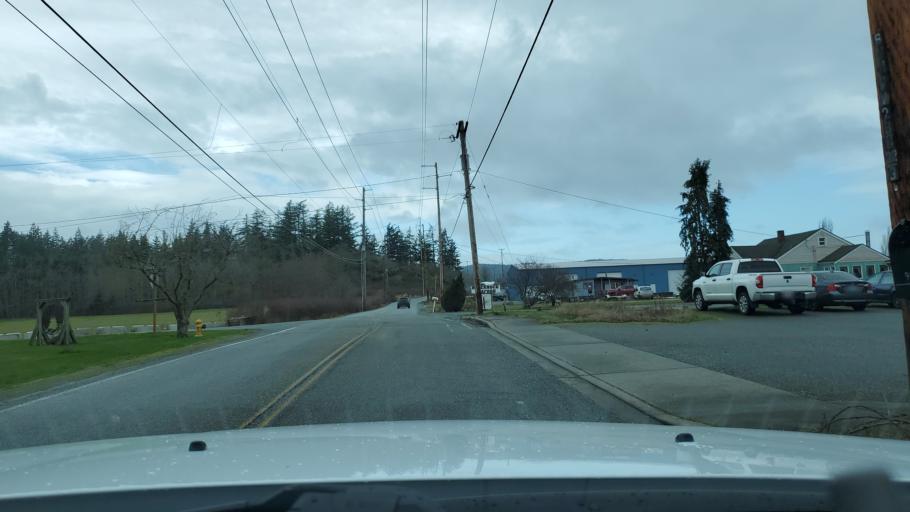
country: US
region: Washington
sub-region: Skagit County
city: Anacortes
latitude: 48.4584
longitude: -122.5488
